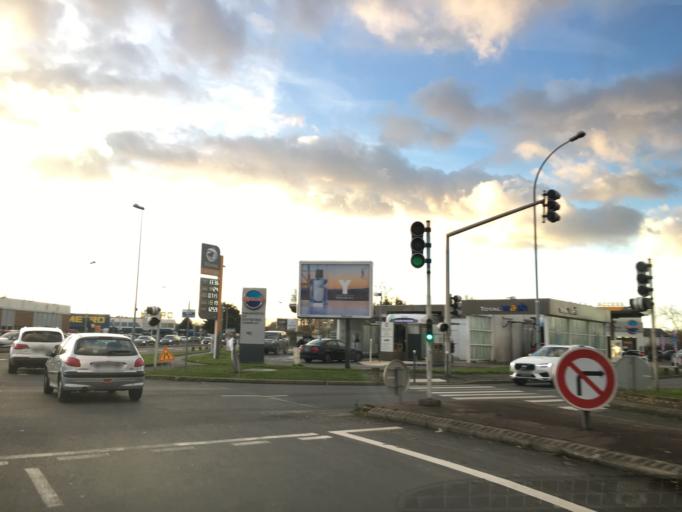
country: FR
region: Ile-de-France
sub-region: Departement du Val-de-Marne
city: Chennevieres-sur-Marne
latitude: 48.7994
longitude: 2.5442
